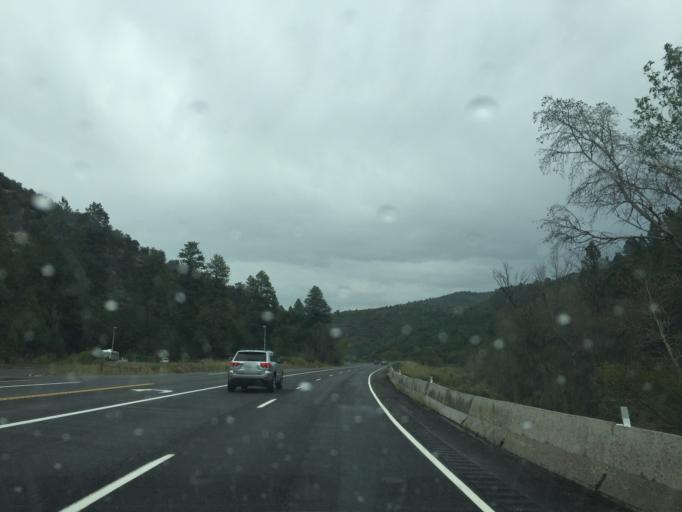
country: US
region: Utah
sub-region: Kane County
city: Kanab
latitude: 37.3789
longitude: -112.5875
